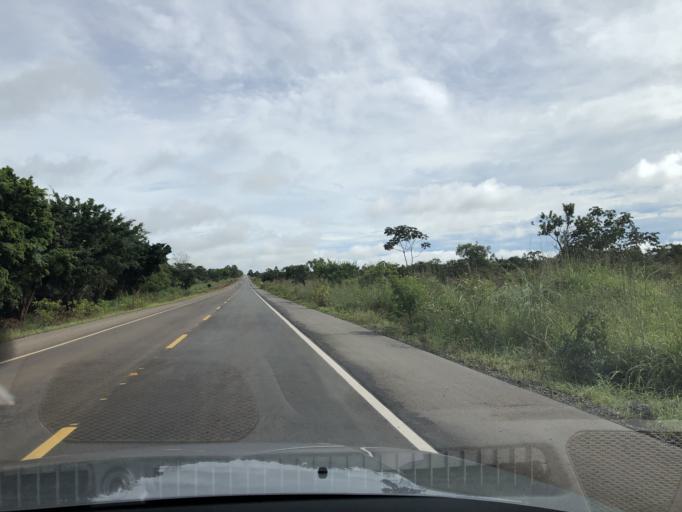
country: BR
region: Federal District
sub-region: Brasilia
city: Brasilia
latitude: -15.6653
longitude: -48.0862
